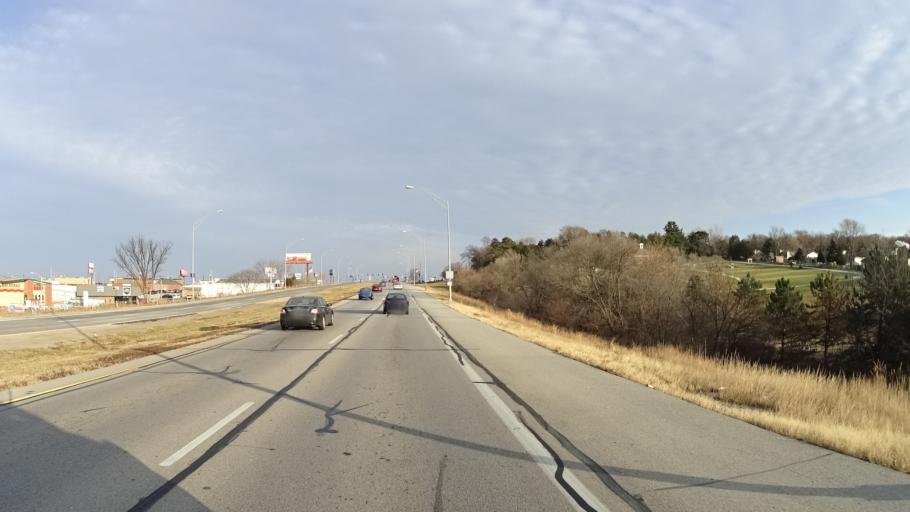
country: US
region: Nebraska
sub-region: Douglas County
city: Ralston
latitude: 41.2124
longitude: -96.0479
